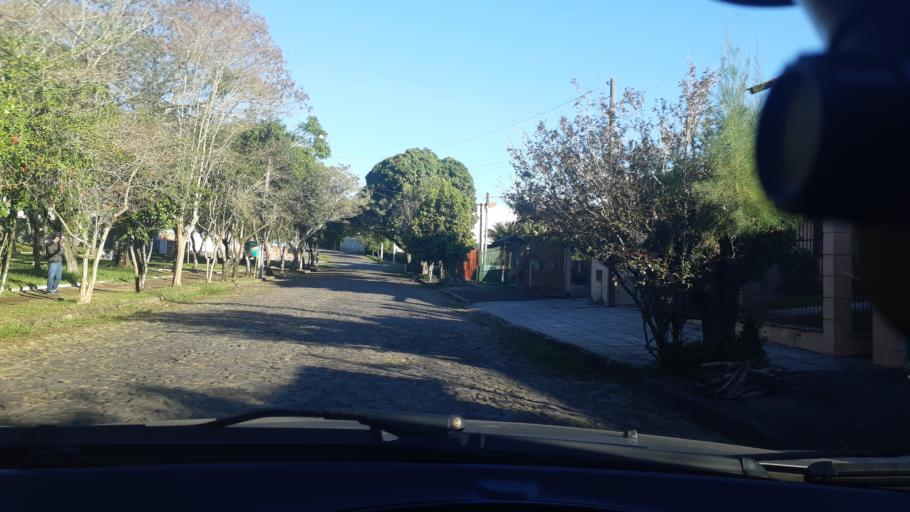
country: BR
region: Rio Grande do Sul
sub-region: Sao Leopoldo
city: Sao Leopoldo
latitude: -29.7783
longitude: -51.1306
